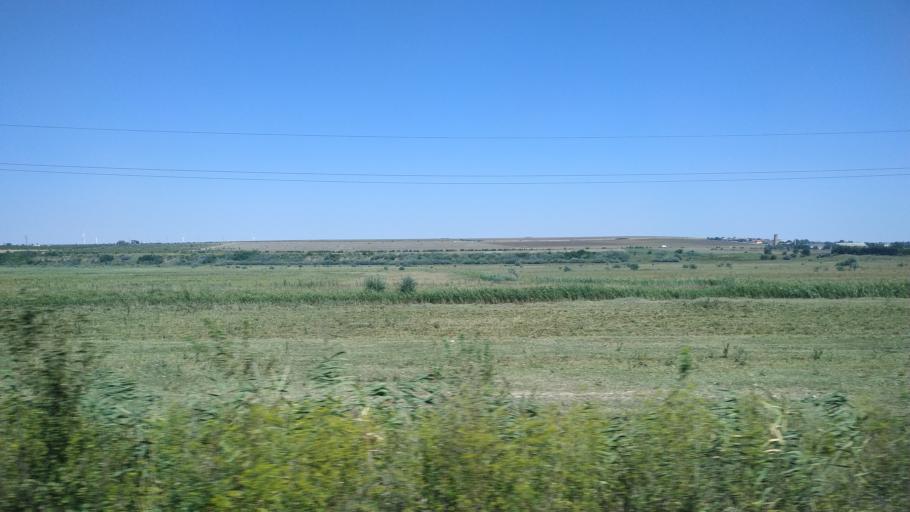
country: RO
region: Constanta
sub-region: Comuna Mircea Voda
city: Satu Nou
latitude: 44.2607
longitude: 28.2066
